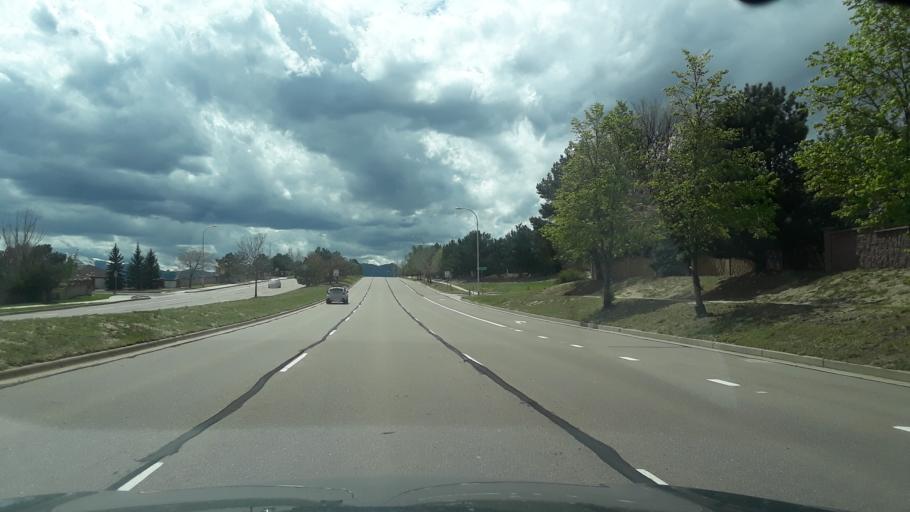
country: US
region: Colorado
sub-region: El Paso County
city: Black Forest
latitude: 38.9569
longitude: -104.7555
